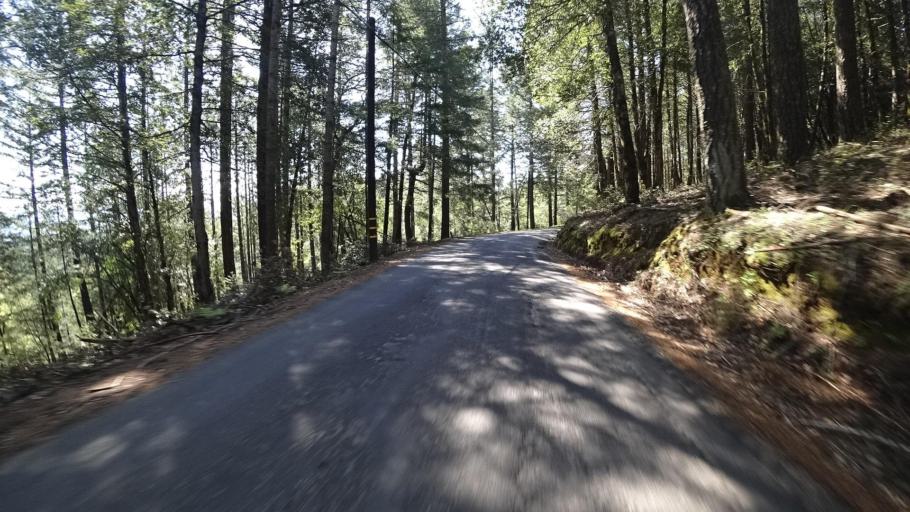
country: US
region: California
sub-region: Humboldt County
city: Redway
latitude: 40.0445
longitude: -123.6404
